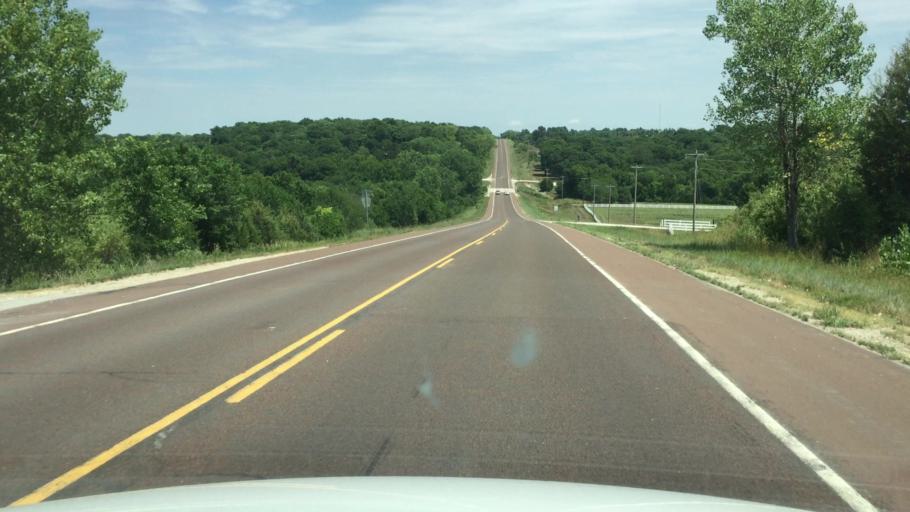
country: US
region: Kansas
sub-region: Douglas County
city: Lawrence
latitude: 38.9713
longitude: -95.3972
